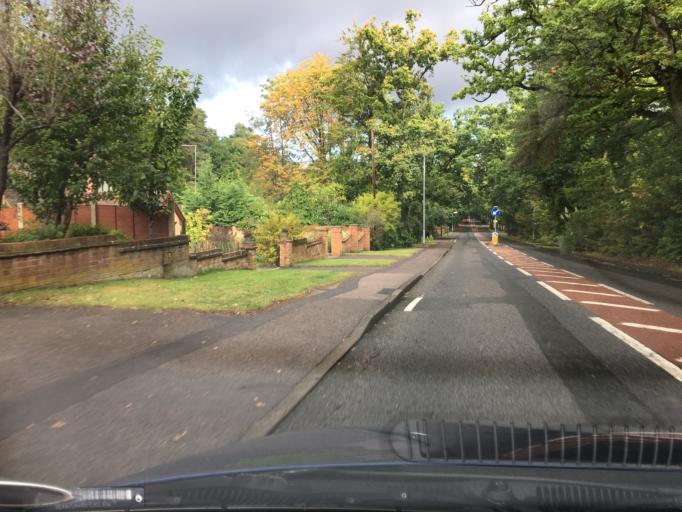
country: GB
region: England
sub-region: Bracknell Forest
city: Crowthorne
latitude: 51.3756
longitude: -0.8044
